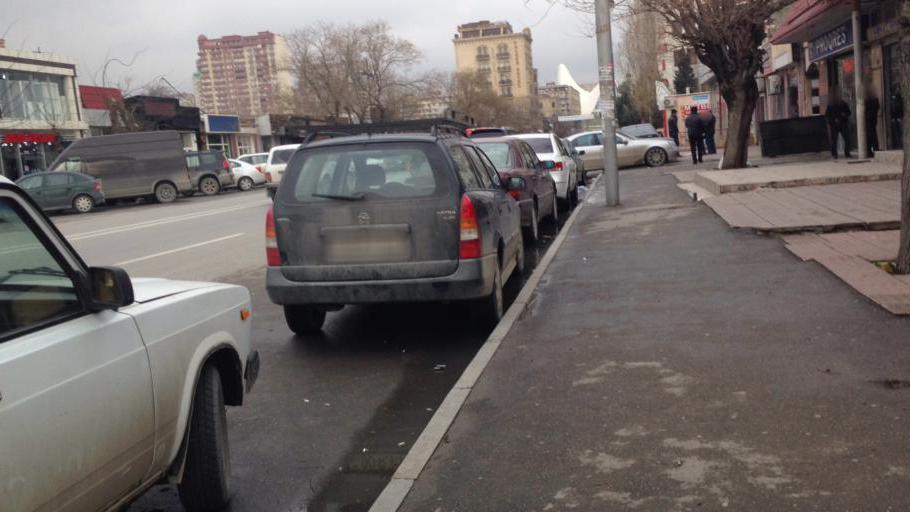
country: AZ
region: Baki
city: Baku
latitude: 40.3884
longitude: 49.8585
